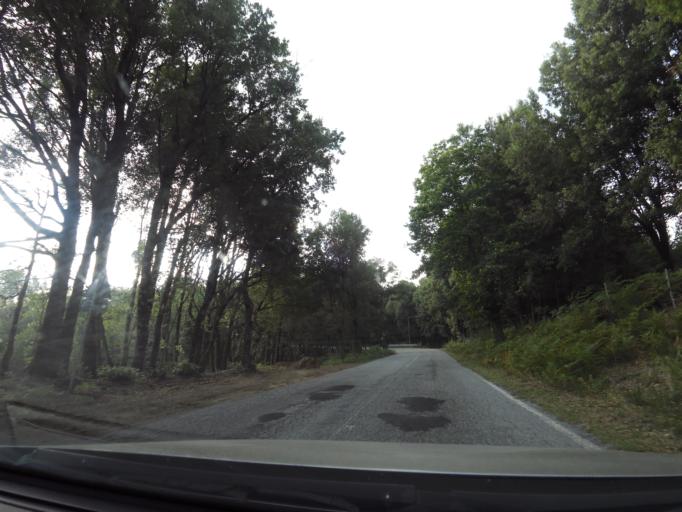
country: IT
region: Calabria
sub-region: Provincia di Vibo-Valentia
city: Nardodipace
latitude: 38.4776
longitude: 16.3920
